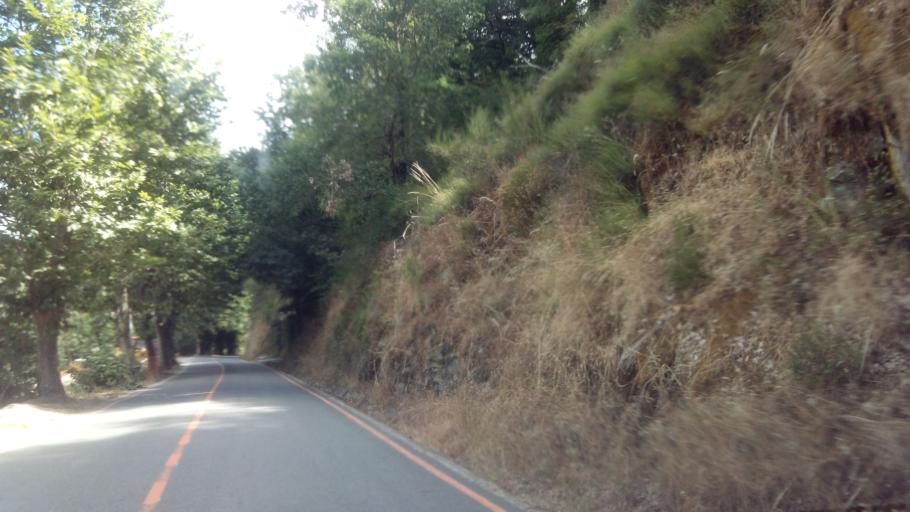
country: ES
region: Galicia
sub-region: Provincia de Ourense
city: Nogueira de Ramuin
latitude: 42.4512
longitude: -7.7322
